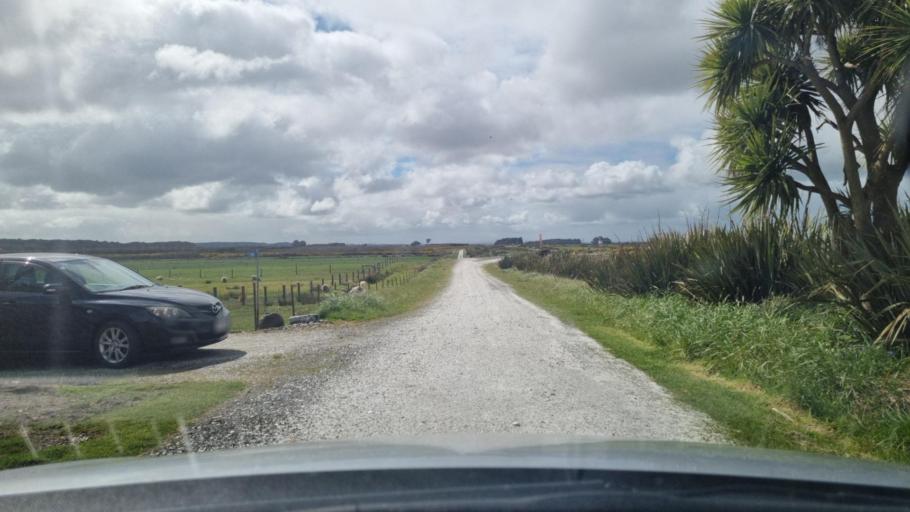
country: NZ
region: Southland
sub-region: Invercargill City
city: Bluff
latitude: -46.5363
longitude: 168.3036
